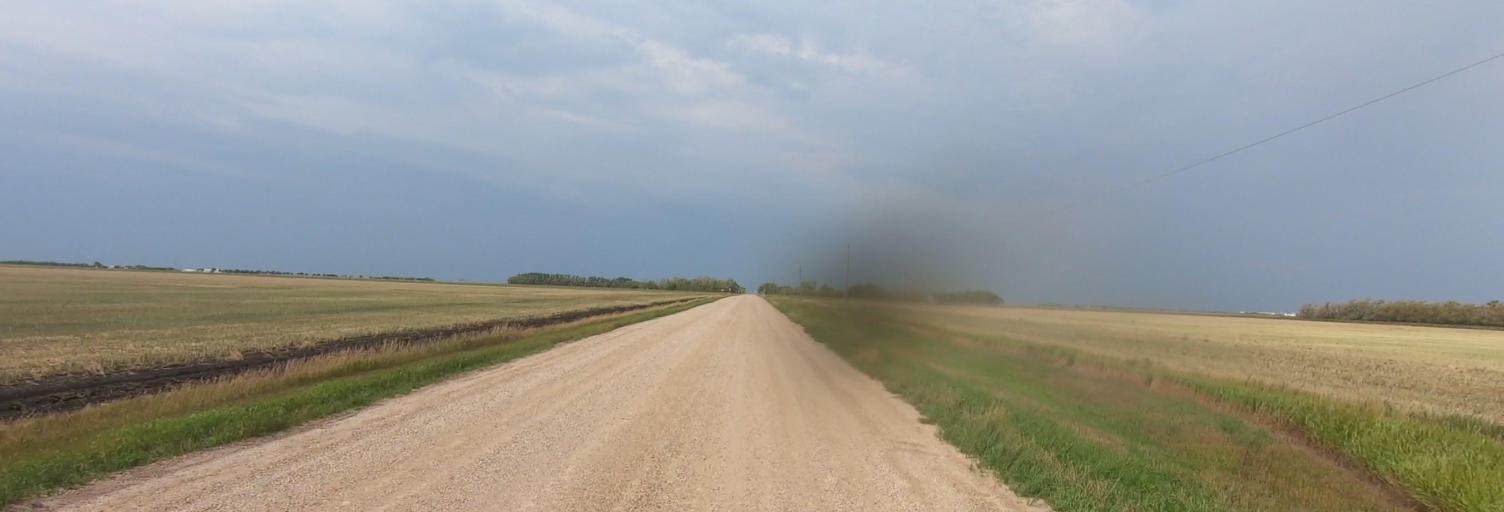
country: CA
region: Manitoba
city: Morris
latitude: 49.5765
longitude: -97.3387
